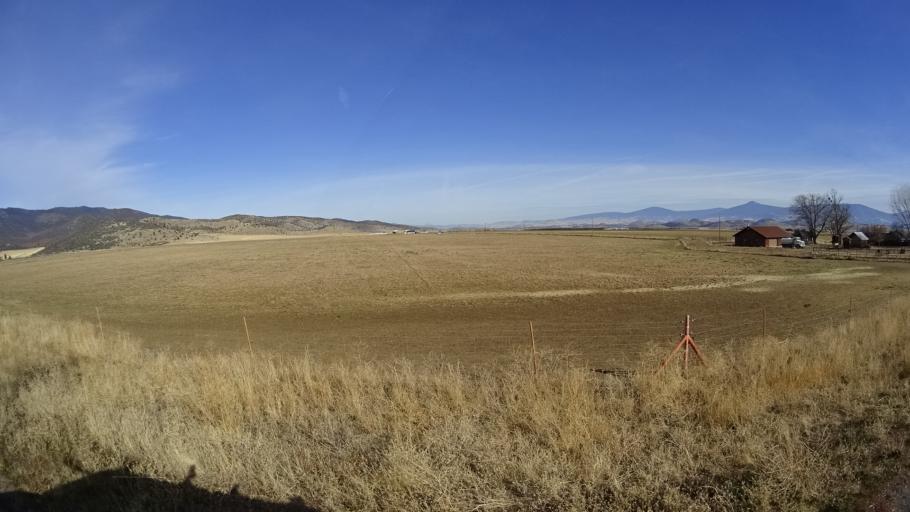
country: US
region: California
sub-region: Siskiyou County
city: Montague
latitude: 41.5382
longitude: -122.5638
